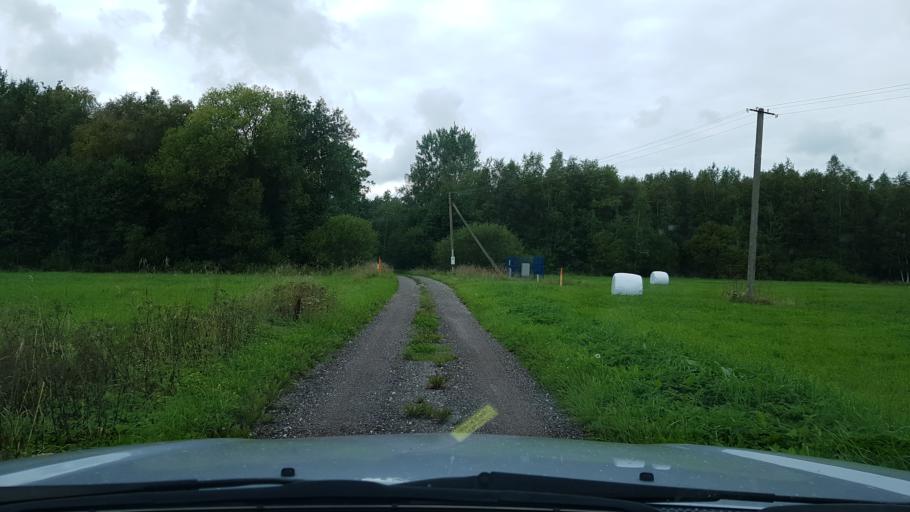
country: EE
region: Harju
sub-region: Joelaehtme vald
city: Loo
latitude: 59.3884
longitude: 24.9706
